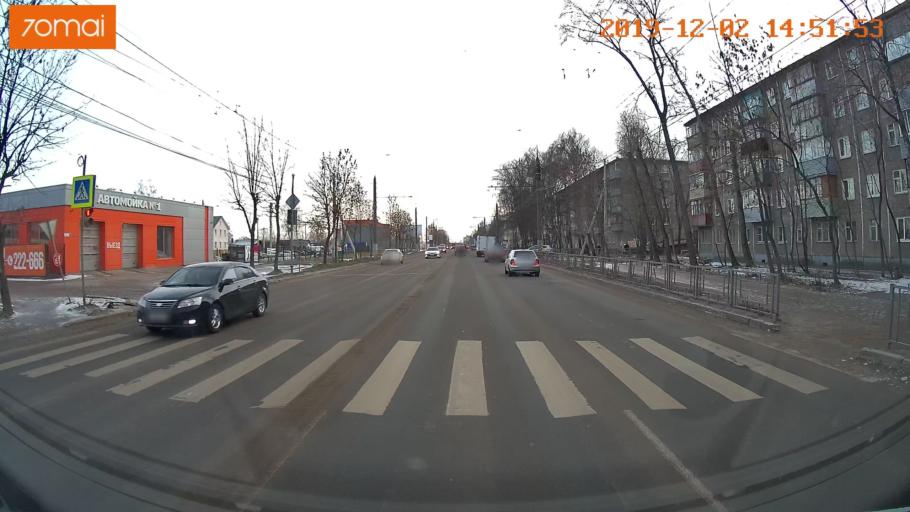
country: RU
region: Ivanovo
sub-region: Gorod Ivanovo
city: Ivanovo
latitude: 56.9736
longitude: 41.0097
